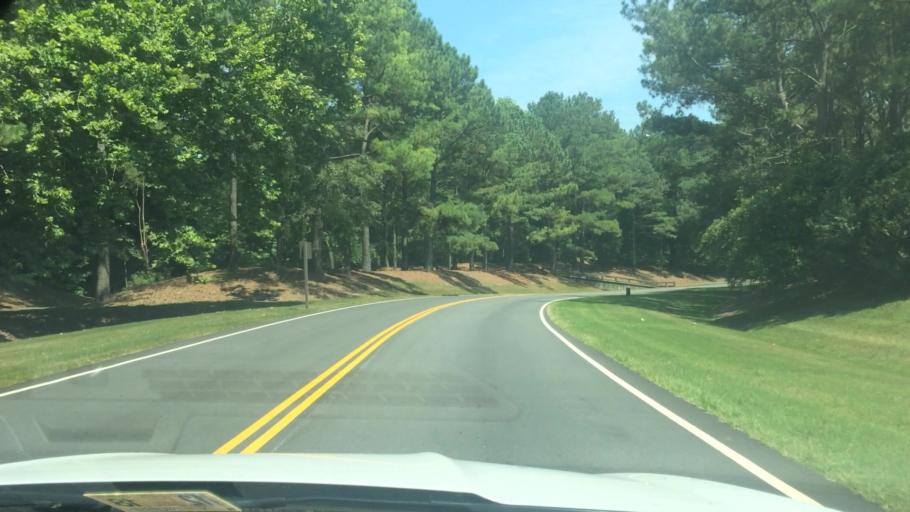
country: US
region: Virginia
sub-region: City of Williamsburg
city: Williamsburg
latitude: 37.2314
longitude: -76.6520
